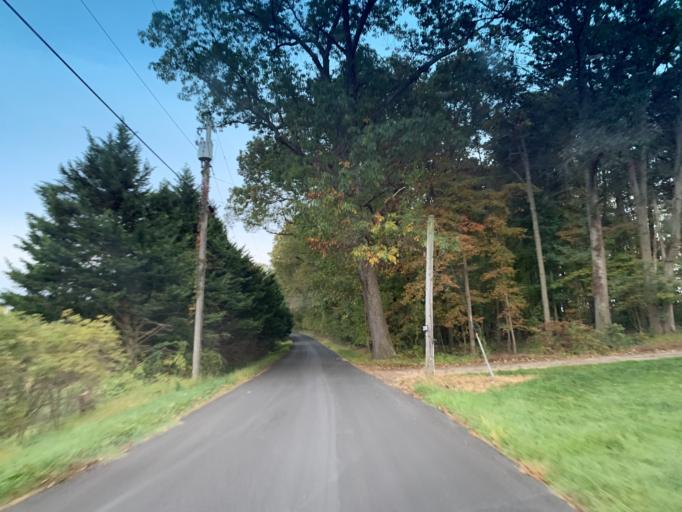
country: US
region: Pennsylvania
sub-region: York County
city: Stewartstown
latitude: 39.6787
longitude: -76.6358
